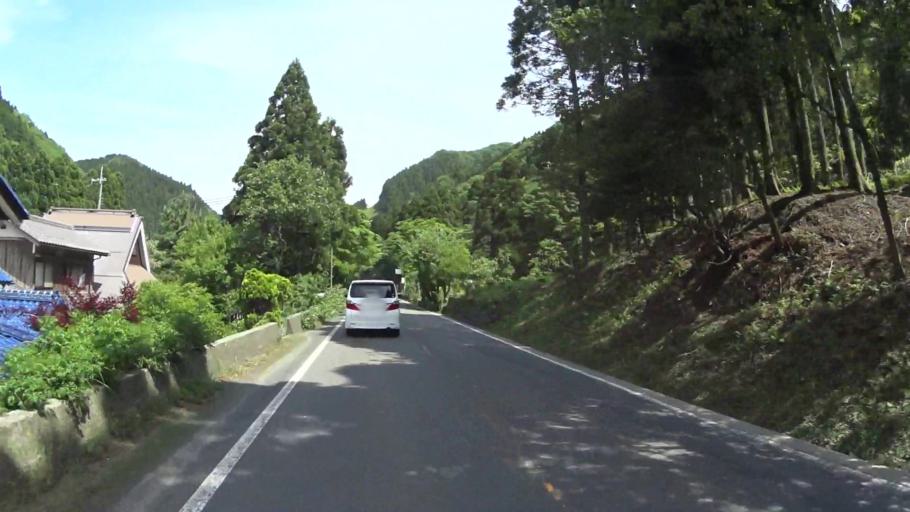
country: JP
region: Fukui
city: Obama
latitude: 35.4384
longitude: 135.9097
